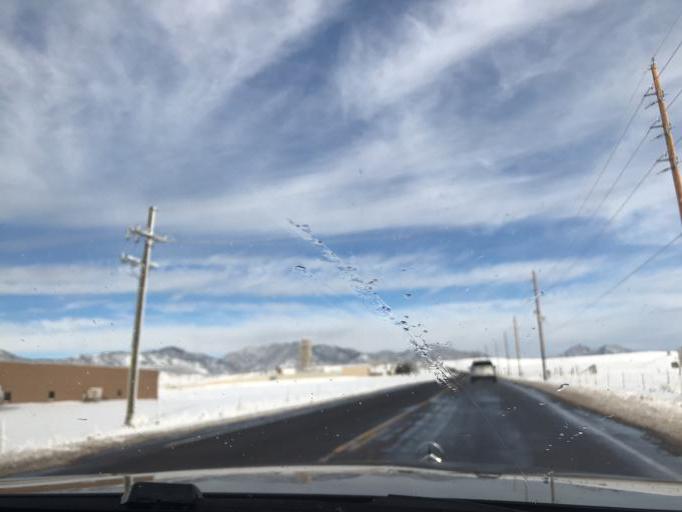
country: US
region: Colorado
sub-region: Boulder County
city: Superior
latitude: 39.8563
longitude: -105.1883
